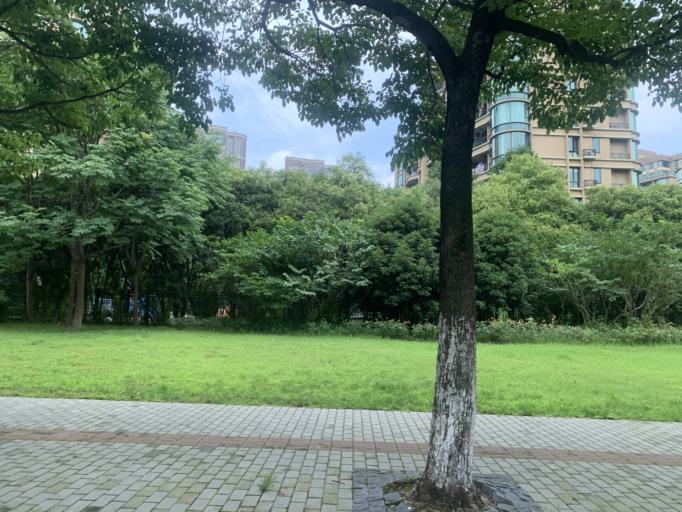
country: CN
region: Shanghai Shi
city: Huamu
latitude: 31.2066
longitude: 121.5313
